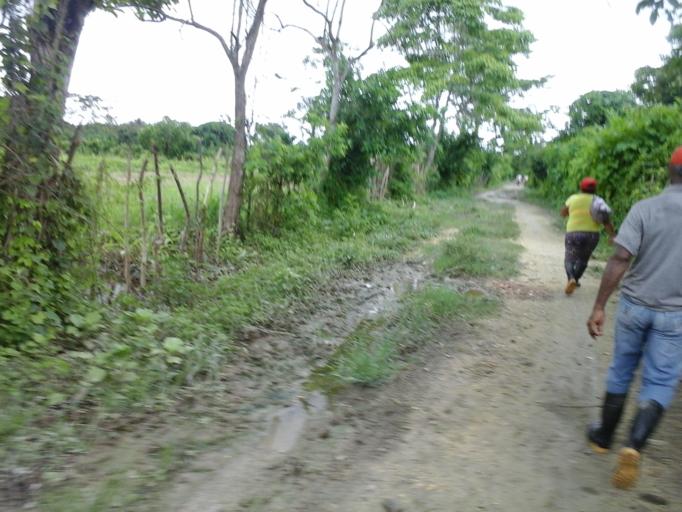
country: CO
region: Bolivar
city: San Pablo
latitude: 10.1545
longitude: -75.2736
